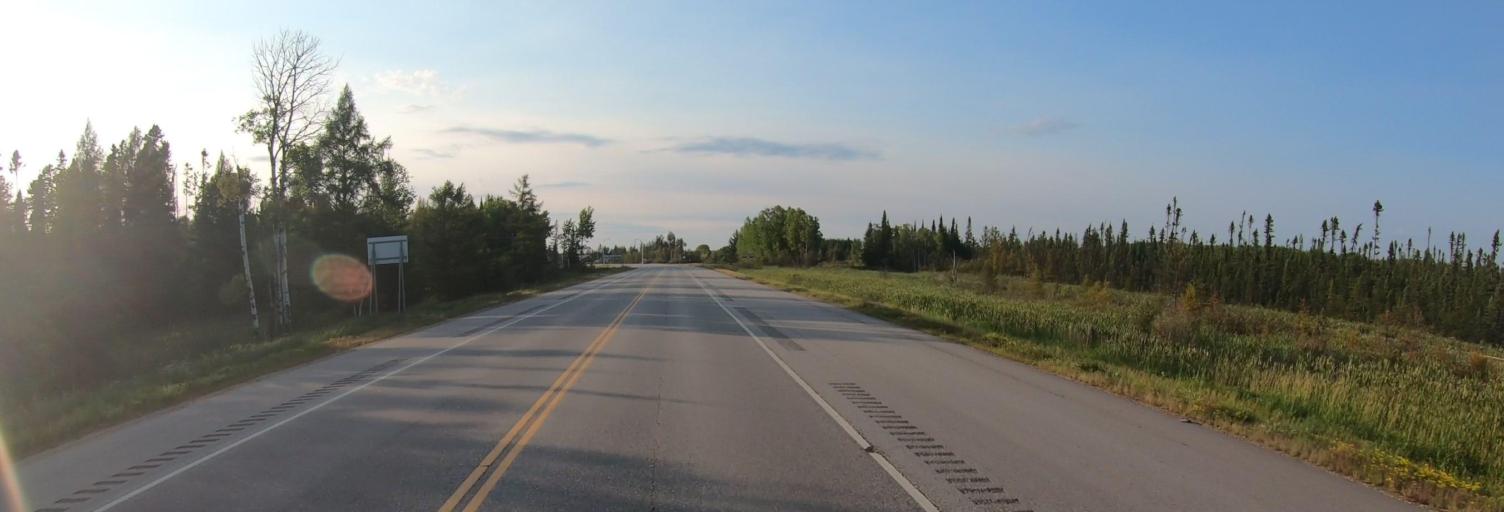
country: US
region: Minnesota
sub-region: Saint Louis County
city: Mountain Iron
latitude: 47.8397
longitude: -92.6775
